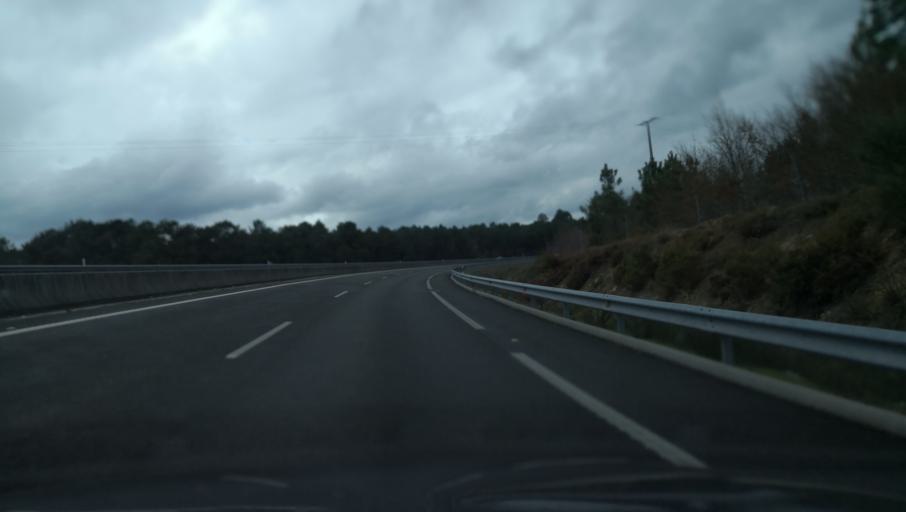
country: ES
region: Galicia
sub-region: Provincia de Ourense
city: Maside
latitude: 42.4331
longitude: -8.0165
